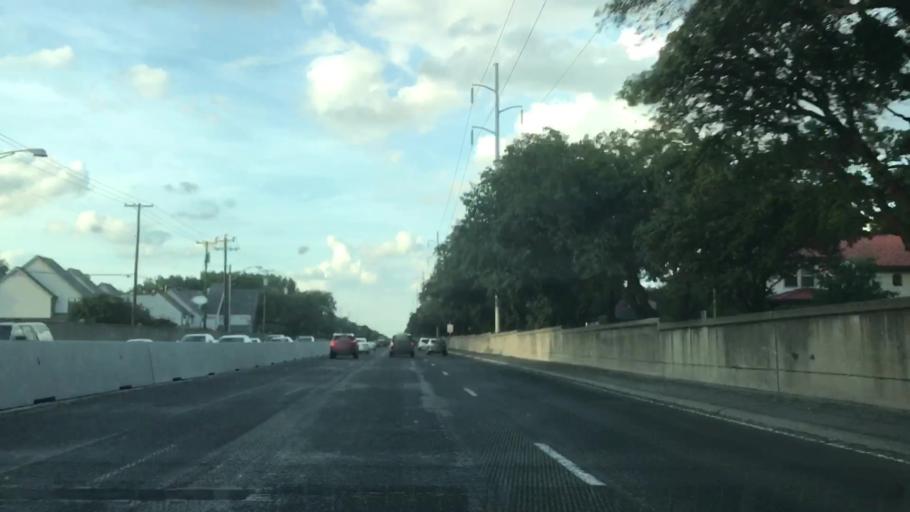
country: US
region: Texas
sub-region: Dallas County
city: Highland Park
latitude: 32.8230
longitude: -96.8166
